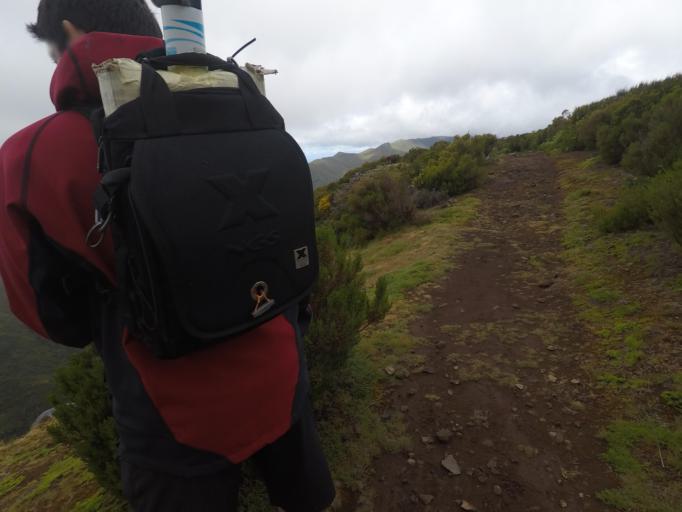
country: PT
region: Madeira
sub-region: Calheta
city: Arco da Calheta
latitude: 32.7731
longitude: -17.1311
